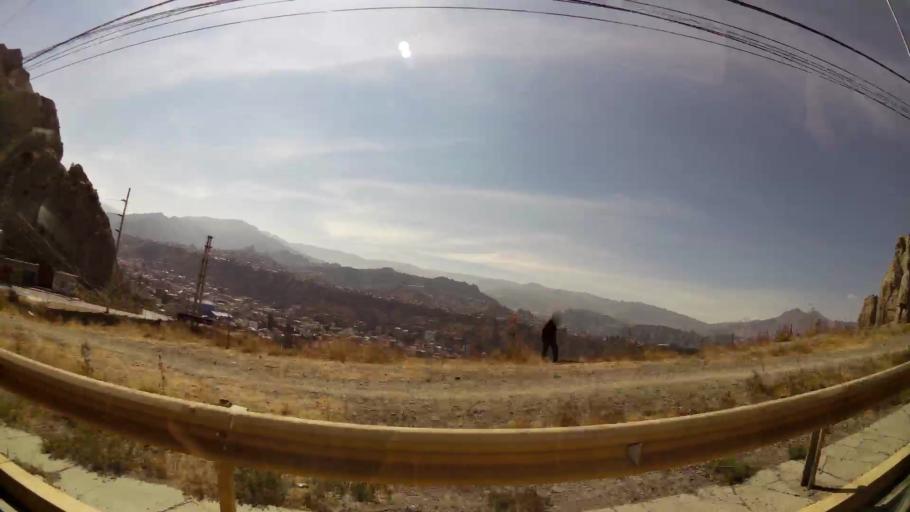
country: BO
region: La Paz
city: La Paz
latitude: -16.5257
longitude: -68.0938
